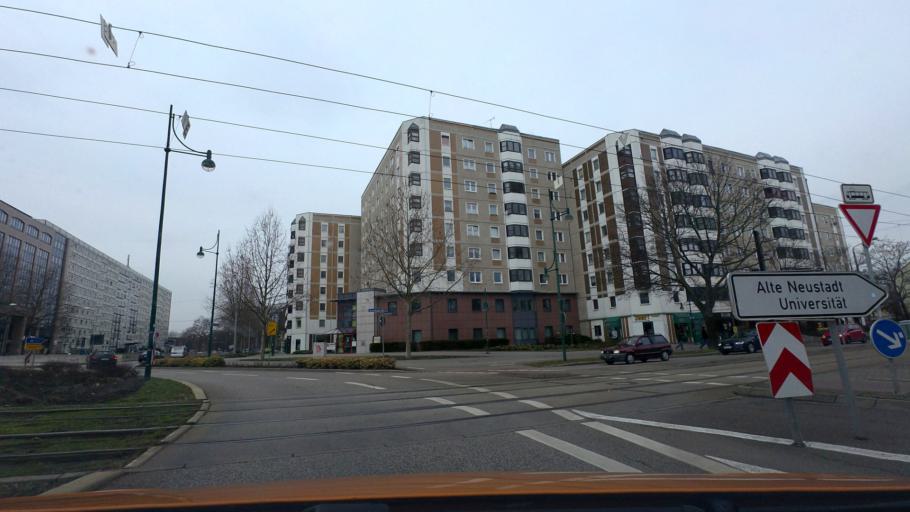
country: DE
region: Saxony-Anhalt
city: Neue Neustadt
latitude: 52.1393
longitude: 11.6399
